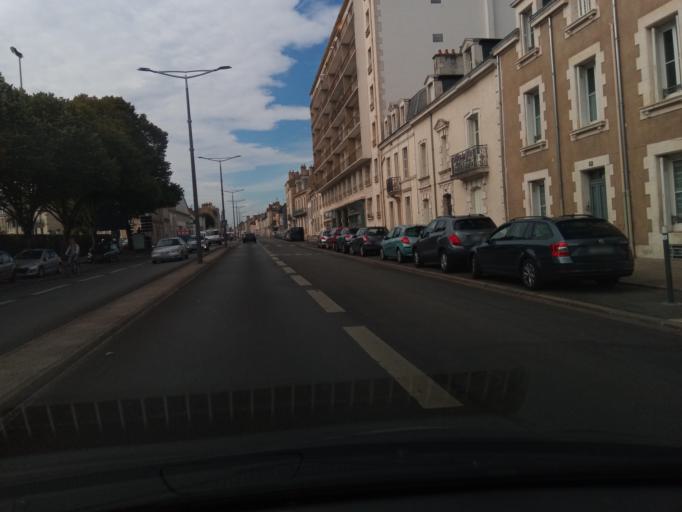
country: FR
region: Poitou-Charentes
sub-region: Departement de la Vienne
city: Poitiers
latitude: 46.5732
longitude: 0.3283
